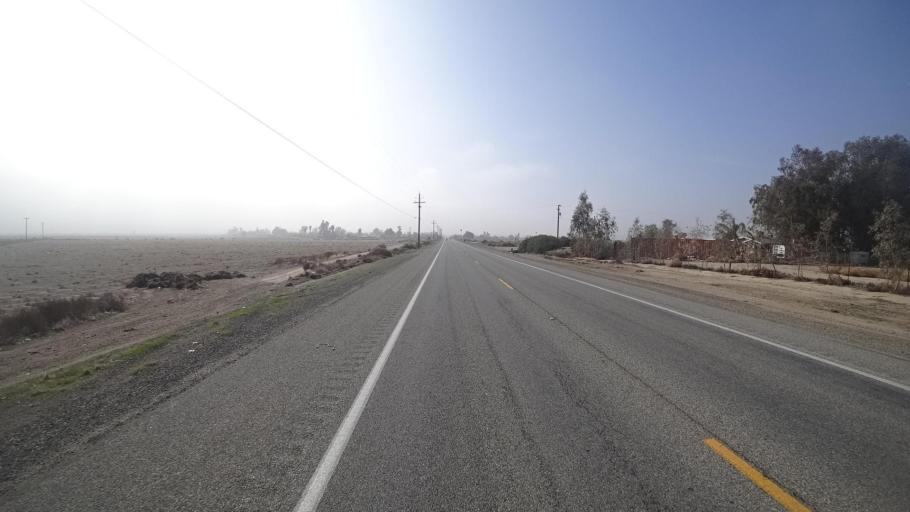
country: US
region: California
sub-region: Kern County
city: Ford City
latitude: 35.2127
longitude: -119.4004
